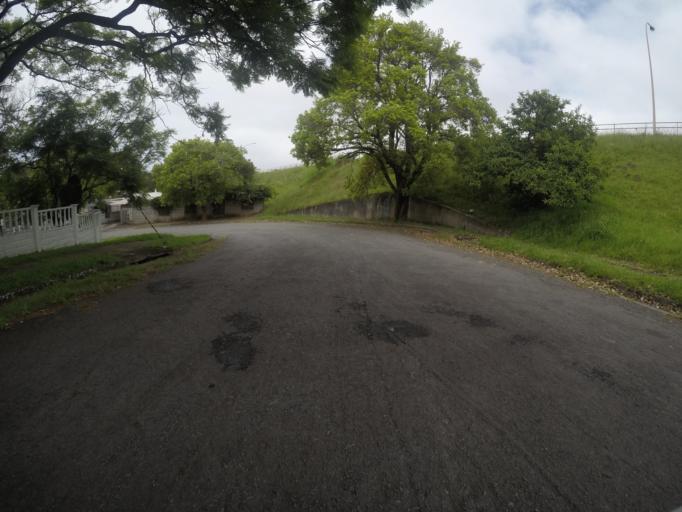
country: ZA
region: Eastern Cape
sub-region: Buffalo City Metropolitan Municipality
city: East London
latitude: -32.9884
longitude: 27.9203
